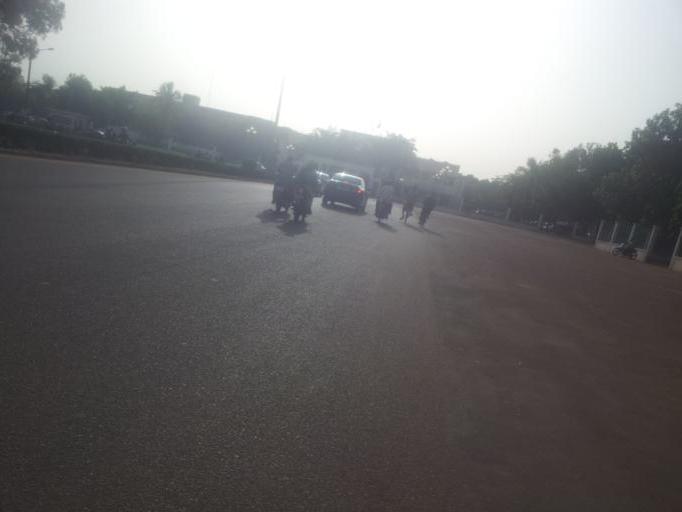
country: BF
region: Centre
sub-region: Kadiogo Province
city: Ouagadougou
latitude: 12.3733
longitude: -1.5107
